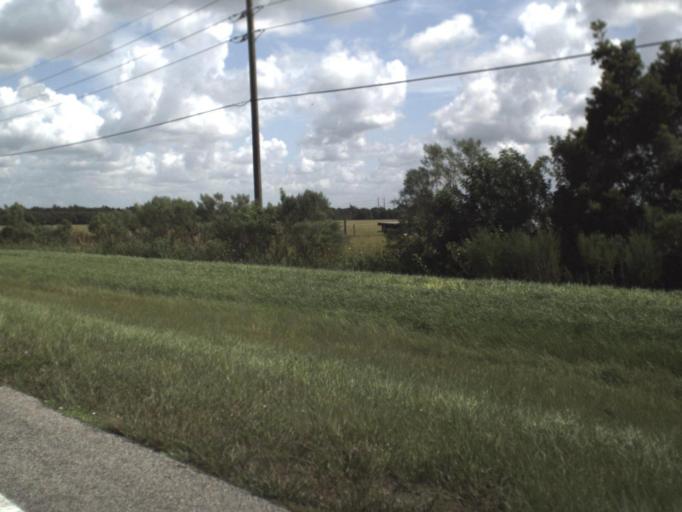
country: US
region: Florida
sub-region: Charlotte County
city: Harbour Heights
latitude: 27.0167
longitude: -81.9585
